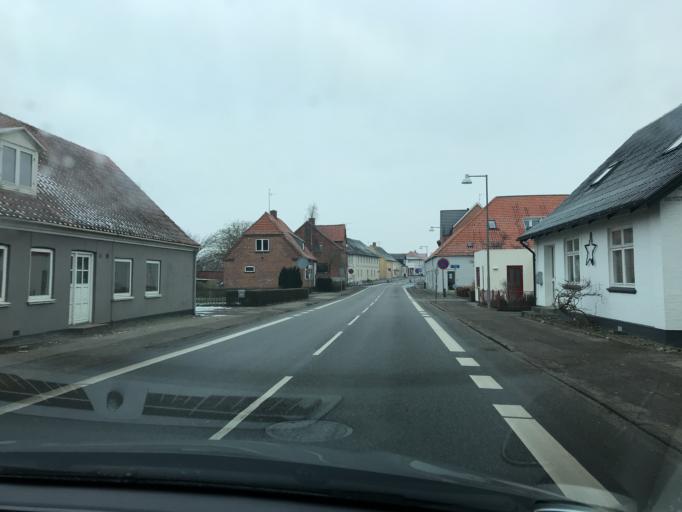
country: DK
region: Zealand
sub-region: Odsherred Kommune
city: Horve
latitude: 55.7515
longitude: 11.4550
